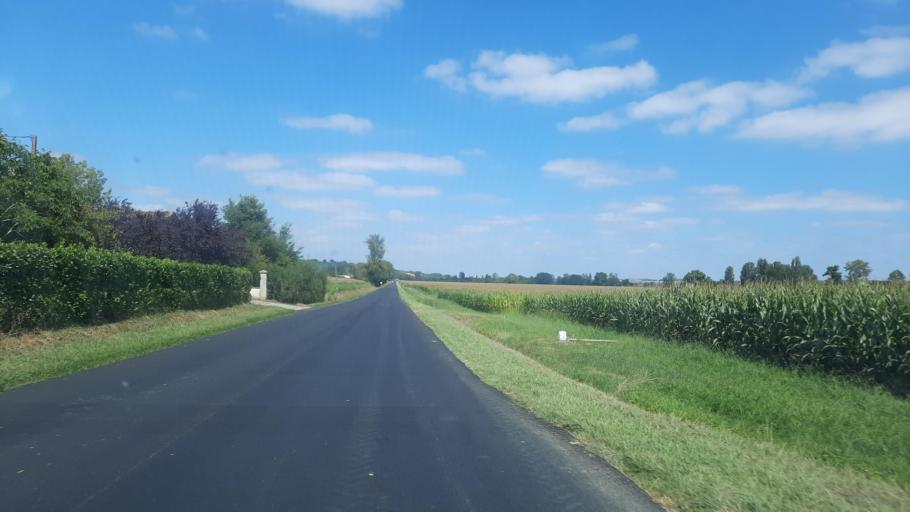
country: FR
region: Midi-Pyrenees
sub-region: Departement du Gers
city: Lombez
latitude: 43.4525
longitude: 0.8753
